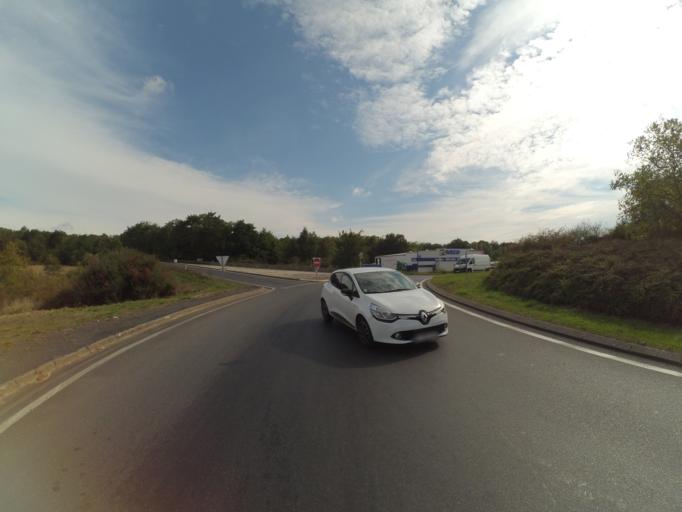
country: FR
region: Pays de la Loire
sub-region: Departement de Maine-et-Loire
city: Distre
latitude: 47.2358
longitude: -0.1119
